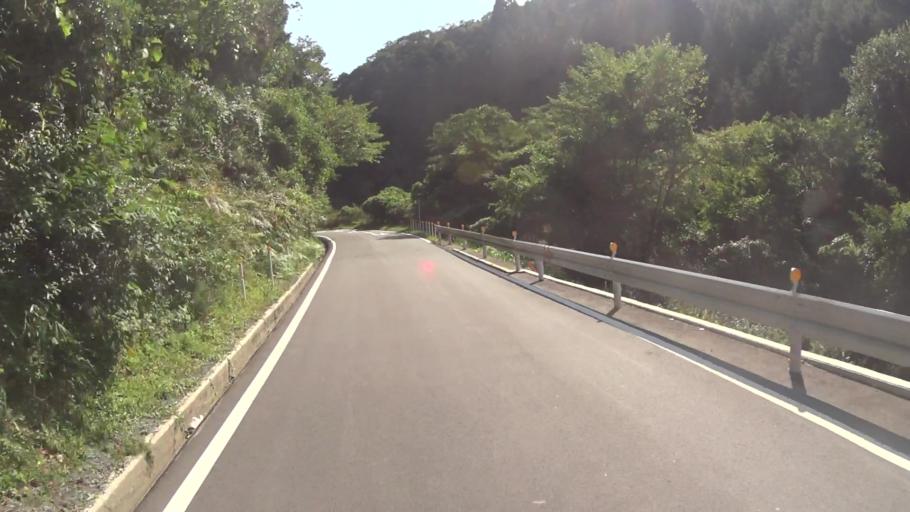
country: JP
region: Kyoto
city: Kameoka
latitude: 34.9828
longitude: 135.5755
